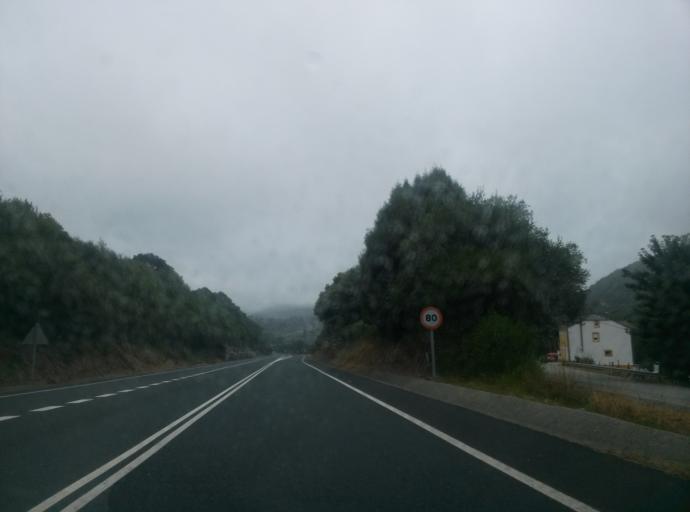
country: ES
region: Galicia
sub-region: Provincia de Lugo
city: Muras
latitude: 43.4459
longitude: -7.7289
